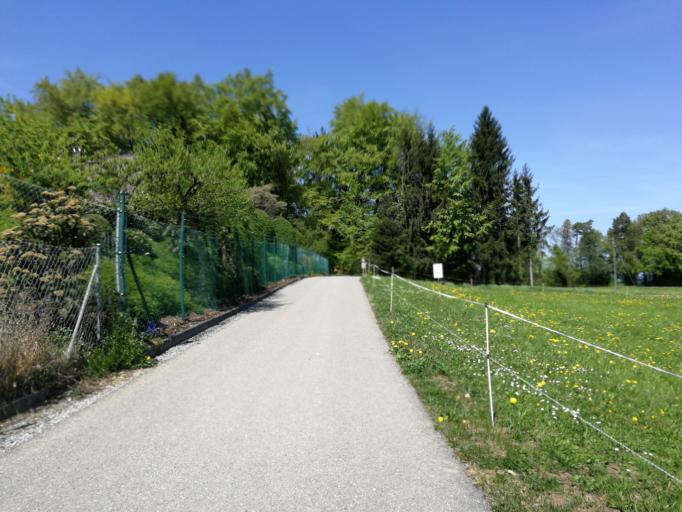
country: CH
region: Zurich
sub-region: Bezirk Meilen
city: Hombrechtikon
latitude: 47.2571
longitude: 8.7569
